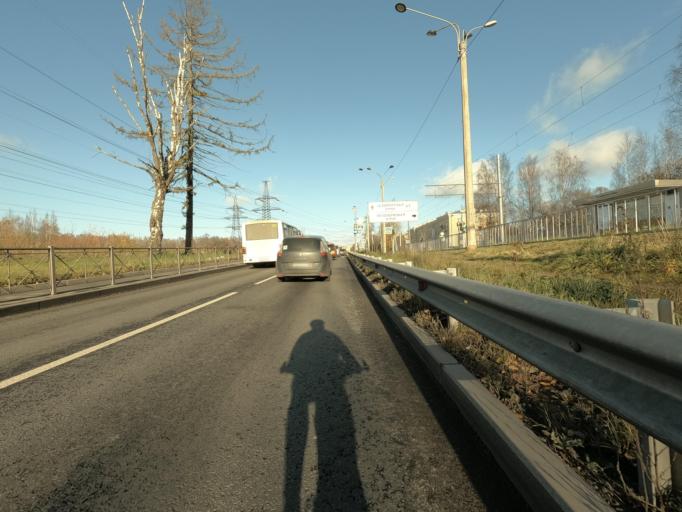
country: RU
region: St.-Petersburg
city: Krasnogvargeisky
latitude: 59.9685
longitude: 30.5029
